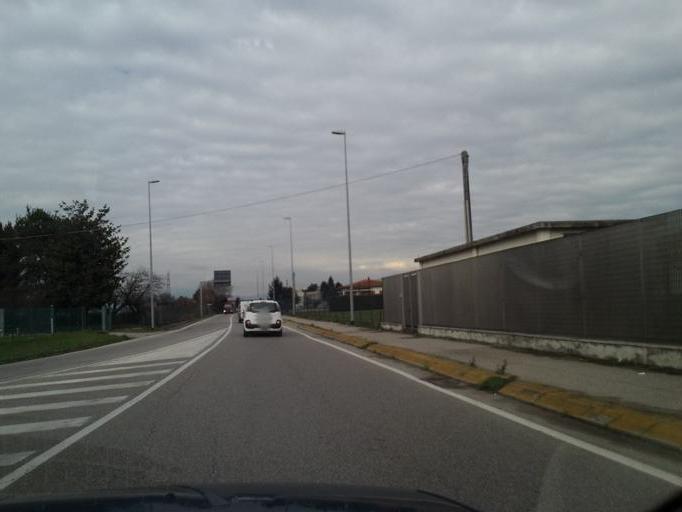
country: IT
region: Veneto
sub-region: Provincia di Verona
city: Villafranca di Verona
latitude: 45.3616
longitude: 10.8452
